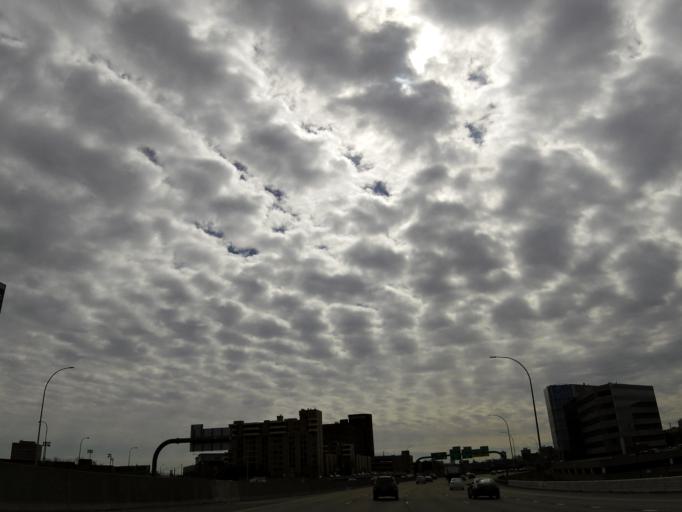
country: US
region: Minnesota
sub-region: Hennepin County
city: Minneapolis
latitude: 44.9774
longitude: -93.2458
